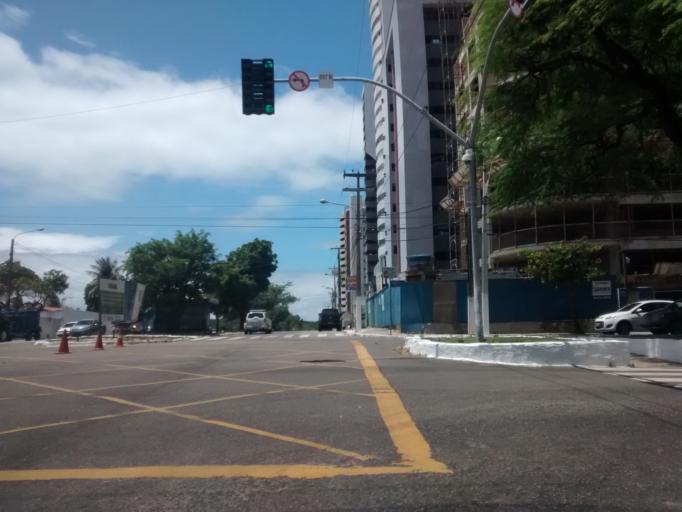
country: BR
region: Rio Grande do Norte
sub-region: Natal
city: Natal
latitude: -5.8075
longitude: -35.2034
